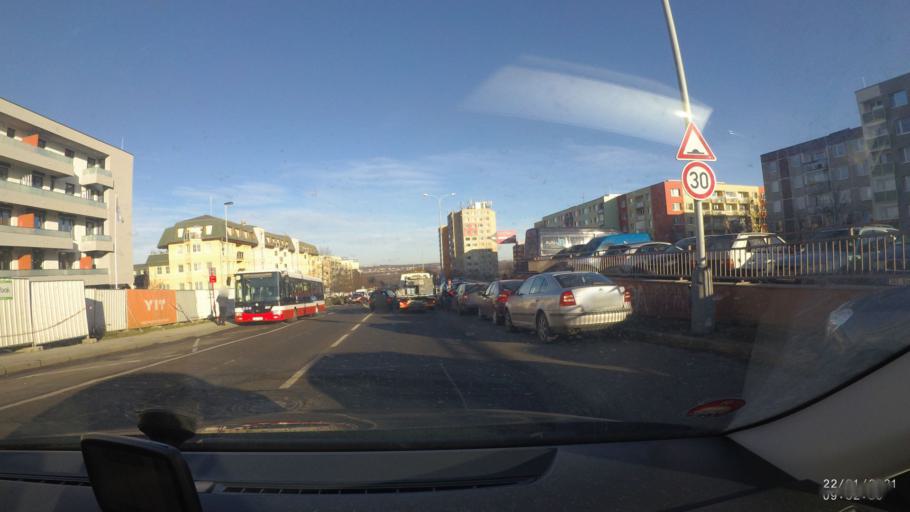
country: CZ
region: Praha
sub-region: Praha 12
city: Modrany
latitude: 50.0280
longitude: 14.3670
